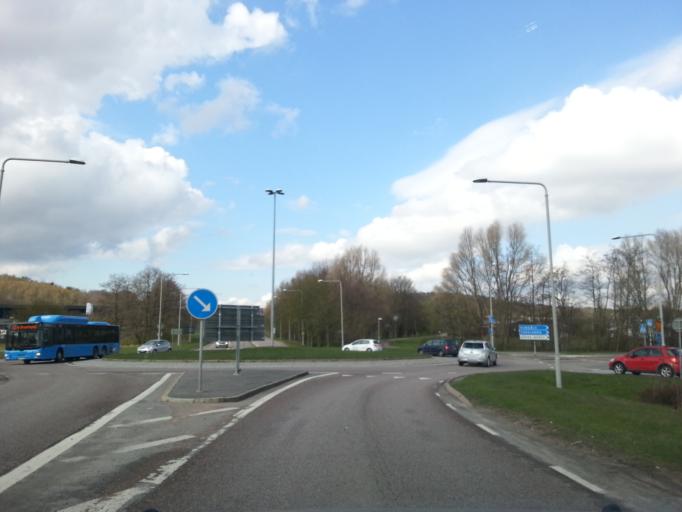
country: SE
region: Vaestra Goetaland
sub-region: Goteborg
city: Gardsten
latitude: 57.7878
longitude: 11.9993
